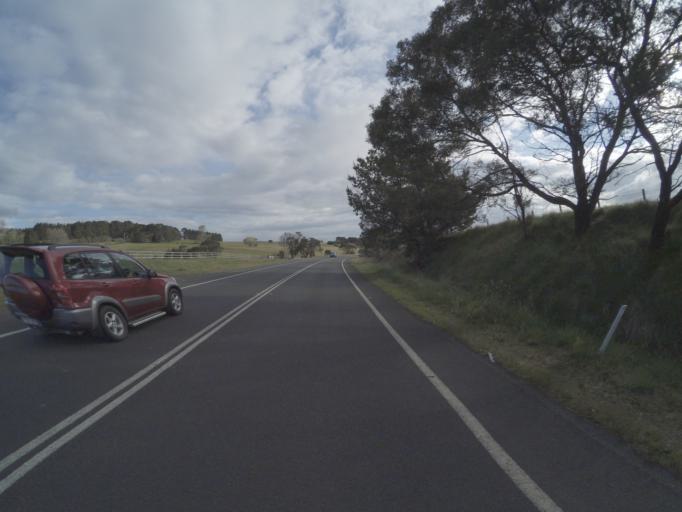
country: AU
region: New South Wales
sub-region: Wingecarribee
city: Bundanoon
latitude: -34.5852
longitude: 150.2962
